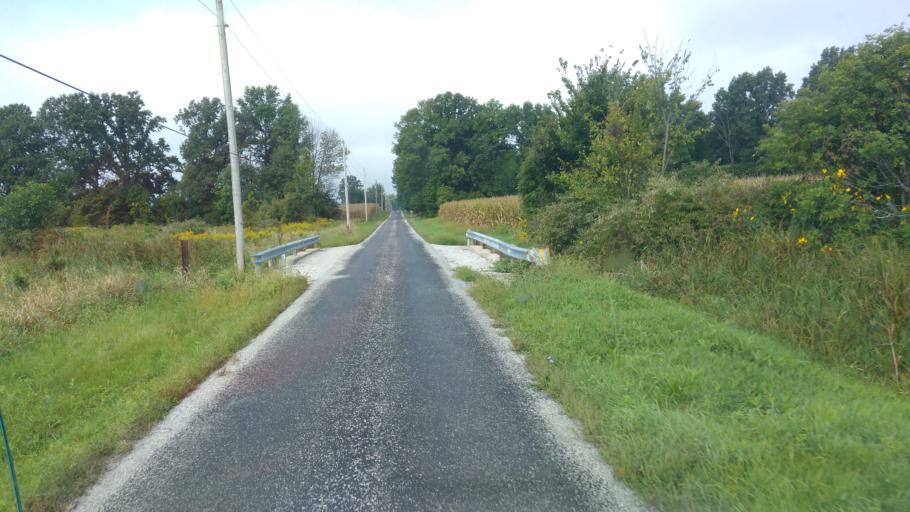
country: US
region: Ohio
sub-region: Morrow County
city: Cardington
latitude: 40.5505
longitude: -82.9775
